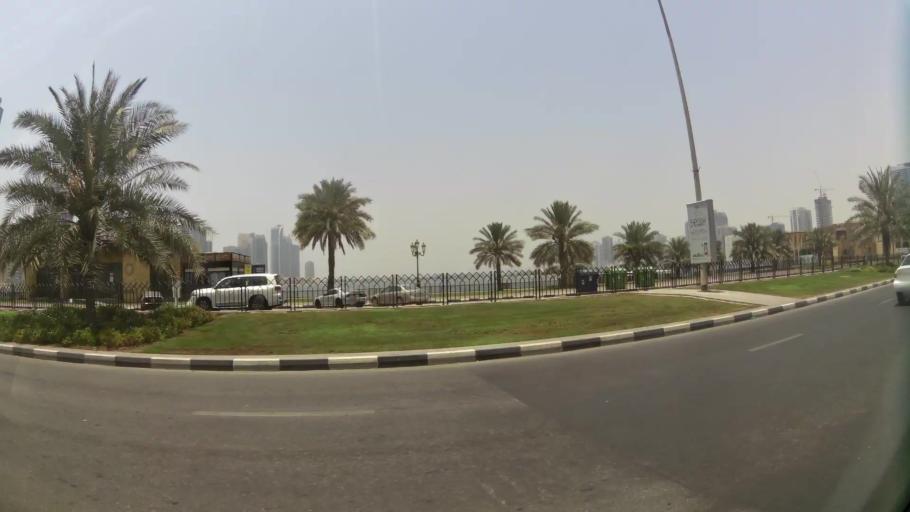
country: AE
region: Ash Shariqah
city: Sharjah
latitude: 25.3244
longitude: 55.3851
